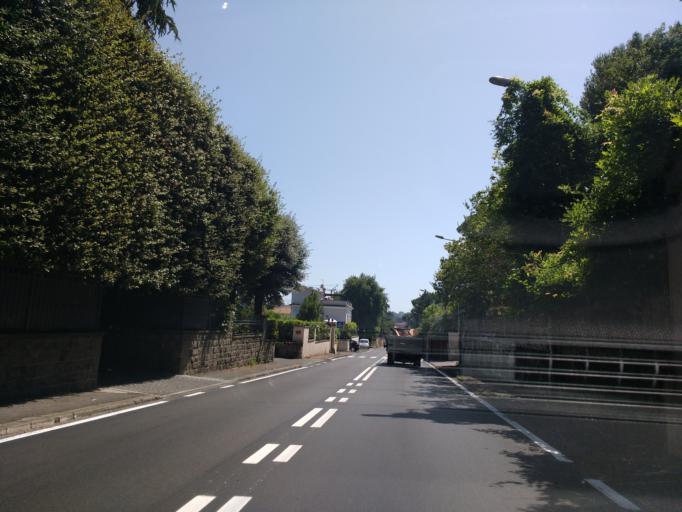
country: IT
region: Latium
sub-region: Citta metropolitana di Roma Capitale
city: Grottaferrata
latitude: 41.7891
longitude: 12.6823
